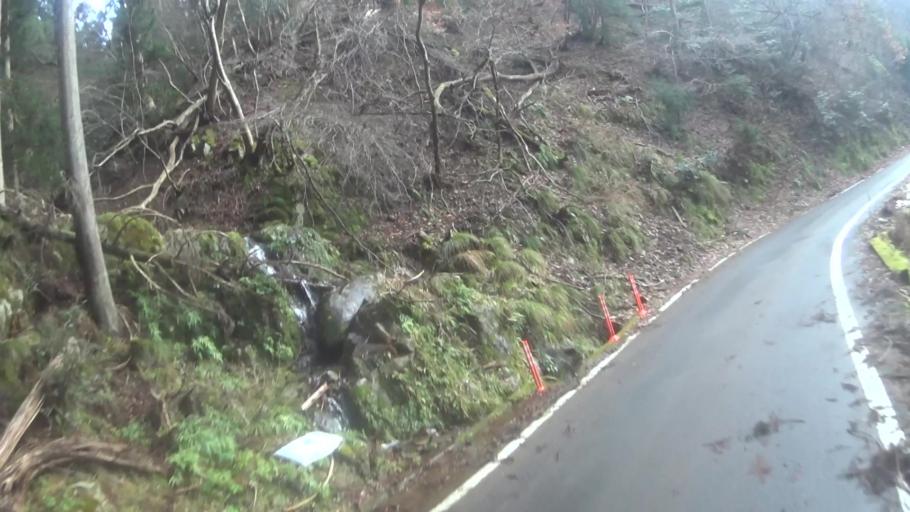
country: JP
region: Kyoto
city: Maizuru
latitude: 35.3667
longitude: 135.4656
